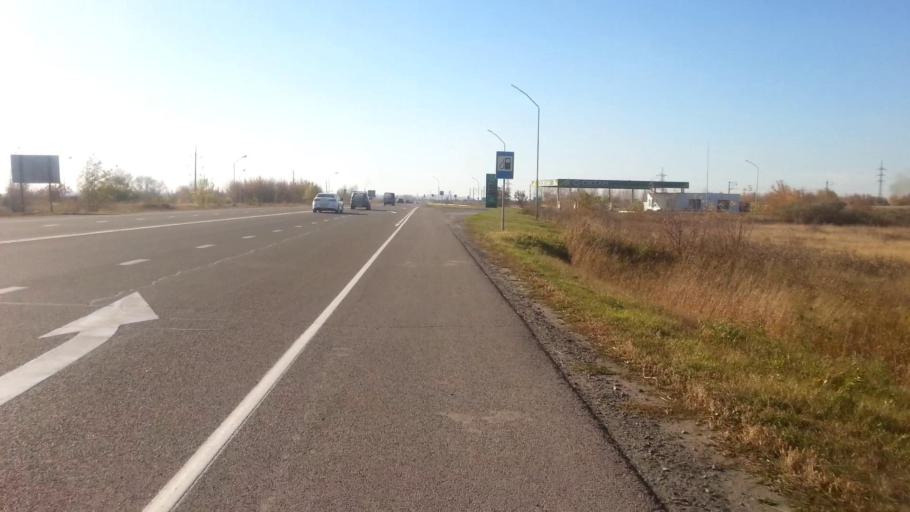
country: RU
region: Altai Krai
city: Novoaltaysk
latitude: 53.3733
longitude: 83.9485
